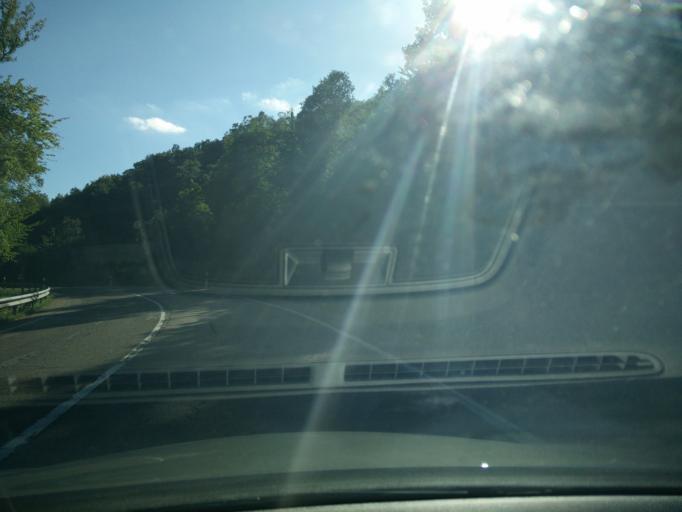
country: ES
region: Castille and Leon
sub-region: Provincia de Leon
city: Cremenes
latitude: 42.9345
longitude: -5.1068
